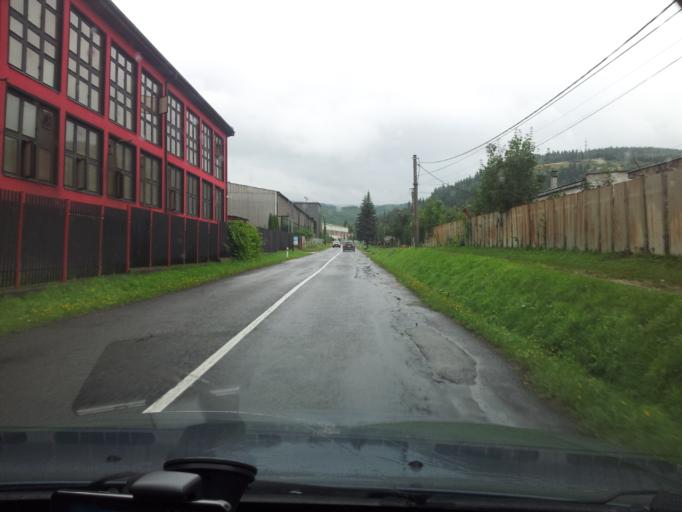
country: SK
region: Banskobystricky
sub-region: Okres Banska Bystrica
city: Brezno
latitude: 48.8137
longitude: 19.5581
